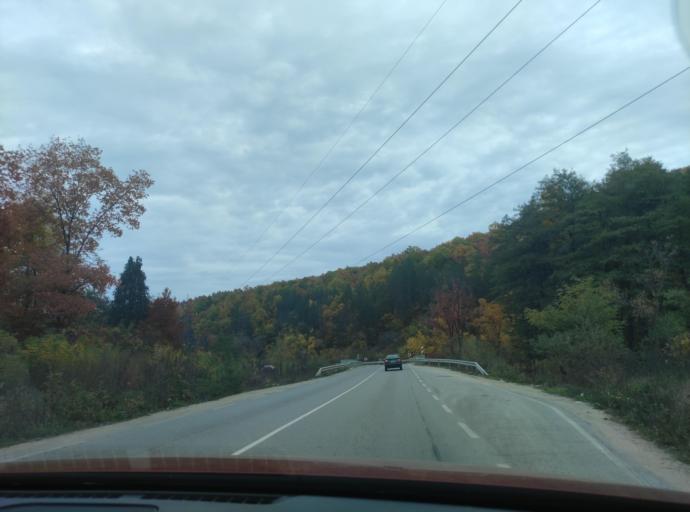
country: BG
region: Montana
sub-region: Obshtina Berkovitsa
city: Berkovitsa
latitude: 43.2614
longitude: 23.1777
